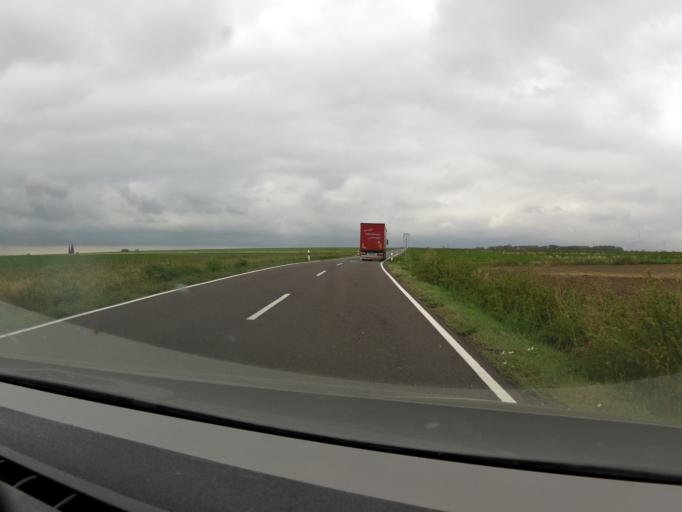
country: DE
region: Saxony-Anhalt
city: Belleben
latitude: 51.6865
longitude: 11.6134
